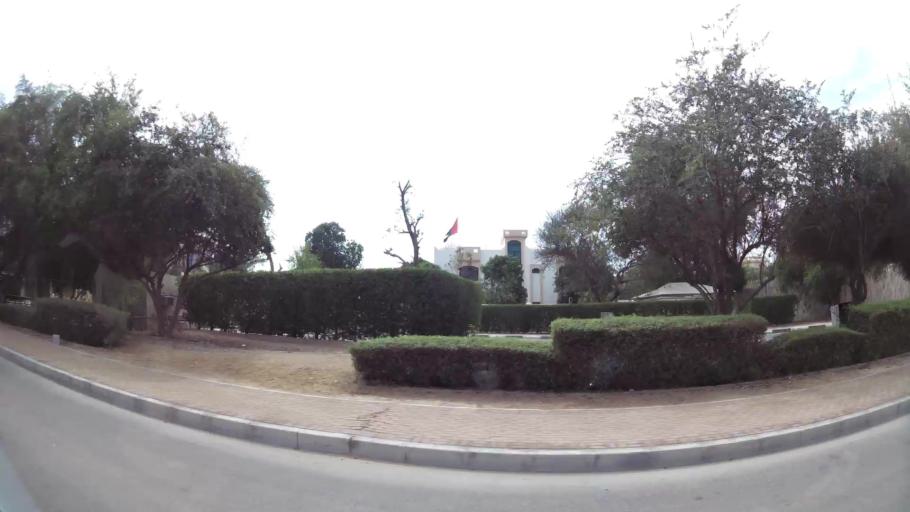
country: OM
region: Al Buraimi
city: Al Buraymi
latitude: 24.2107
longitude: 55.7962
